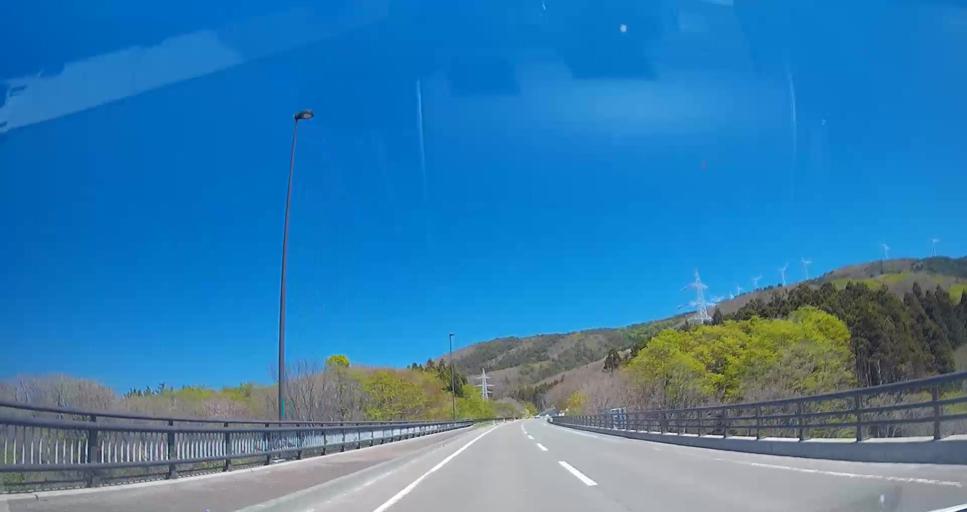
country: JP
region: Aomori
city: Mutsu
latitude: 41.3832
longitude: 141.4058
